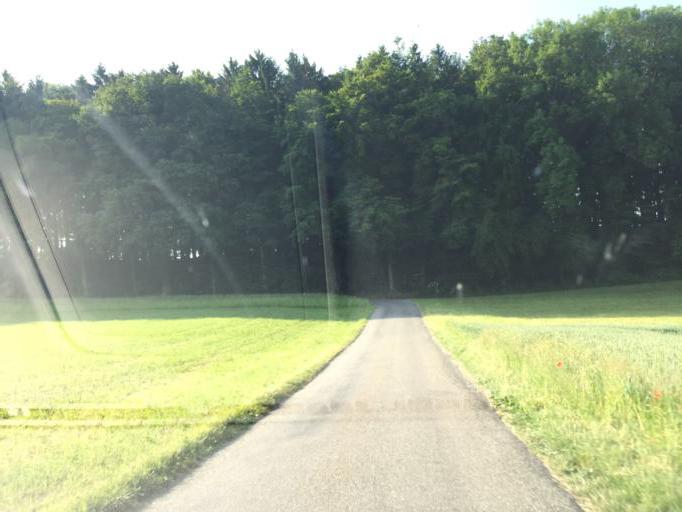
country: CH
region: Zurich
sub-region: Bezirk Buelach
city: Buelach / Gstueckt
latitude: 47.5321
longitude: 8.5585
